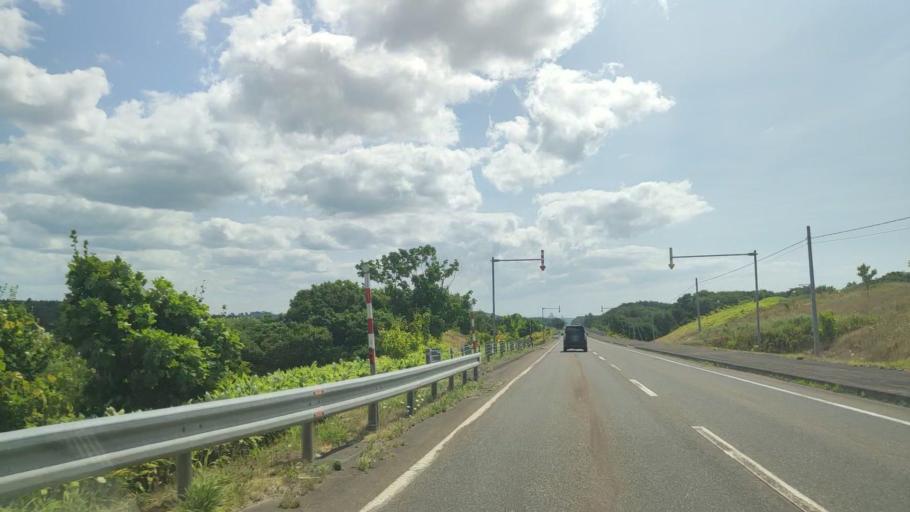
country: JP
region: Hokkaido
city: Makubetsu
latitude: 44.7841
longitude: 141.7904
